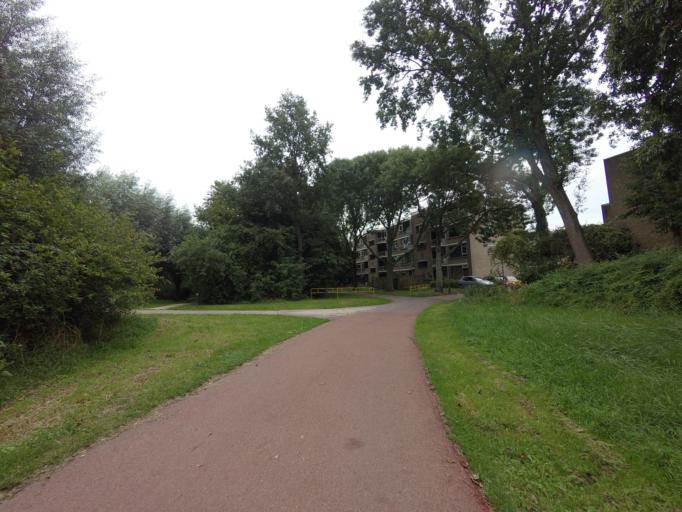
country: NL
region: South Holland
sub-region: Gemeente Alblasserdam
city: Alblasserdam
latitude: 51.8717
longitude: 4.6517
